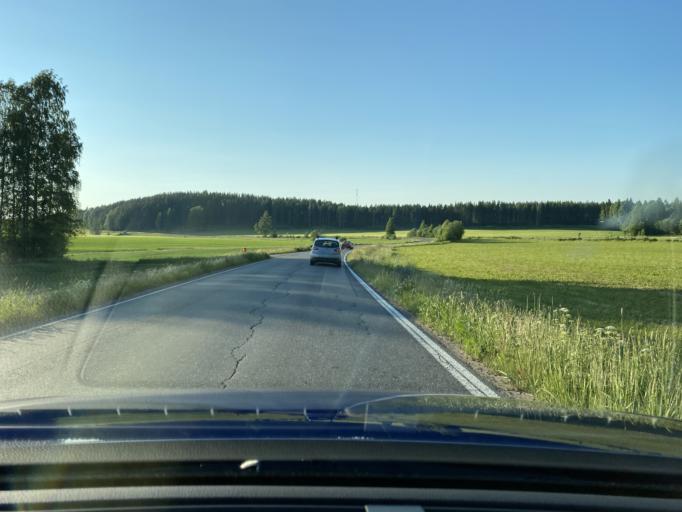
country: FI
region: Haeme
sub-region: Haemeenlinna
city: Tervakoski
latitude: 60.7335
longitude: 24.6699
